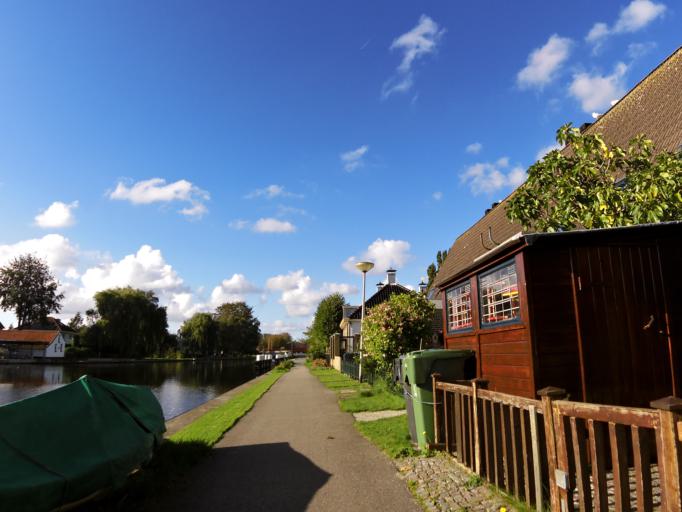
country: NL
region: South Holland
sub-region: Gemeente Leiderdorp
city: Leiderdorp
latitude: 52.1452
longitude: 4.5259
